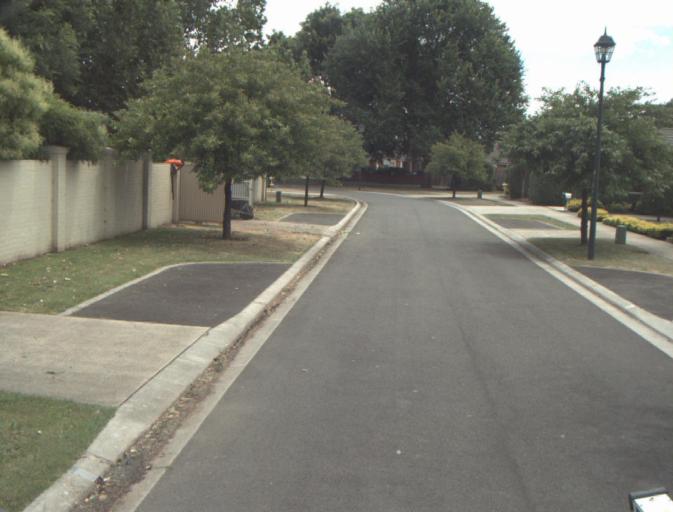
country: AU
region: Tasmania
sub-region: Launceston
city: East Launceston
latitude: -41.4343
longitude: 147.1573
